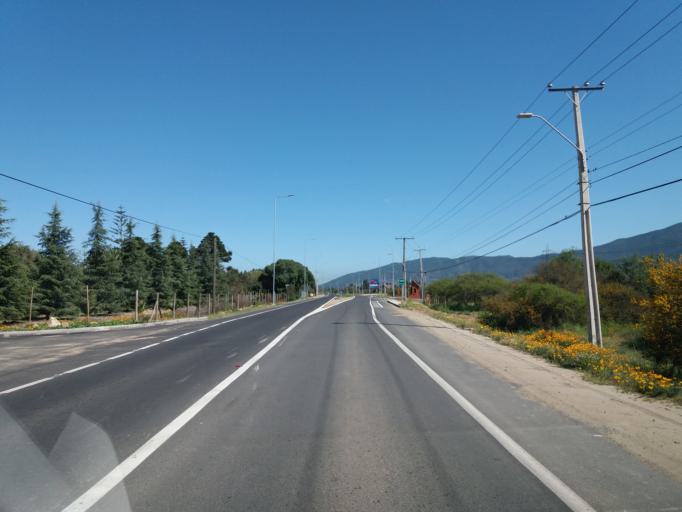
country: CL
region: Valparaiso
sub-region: Provincia de Marga Marga
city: Limache
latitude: -33.0212
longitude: -71.1687
